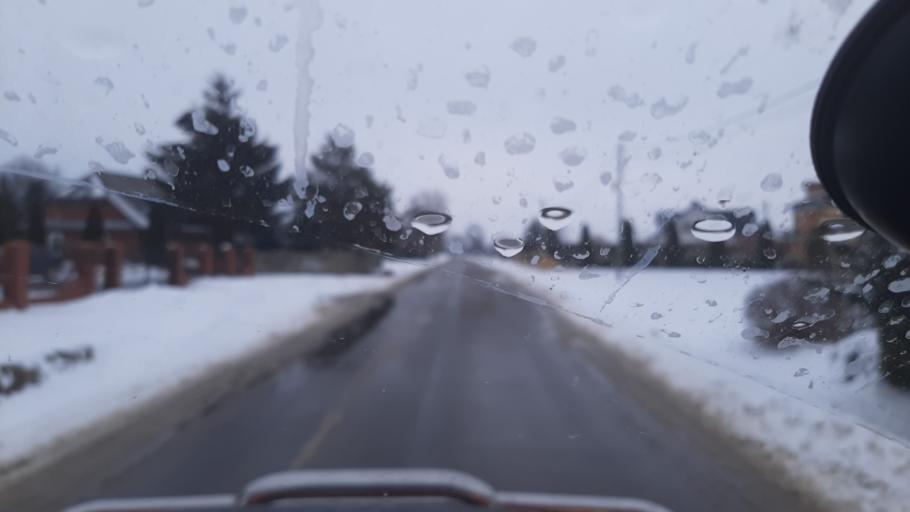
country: PL
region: Lublin Voivodeship
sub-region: Powiat lubelski
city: Jastkow
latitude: 51.3525
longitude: 22.4007
